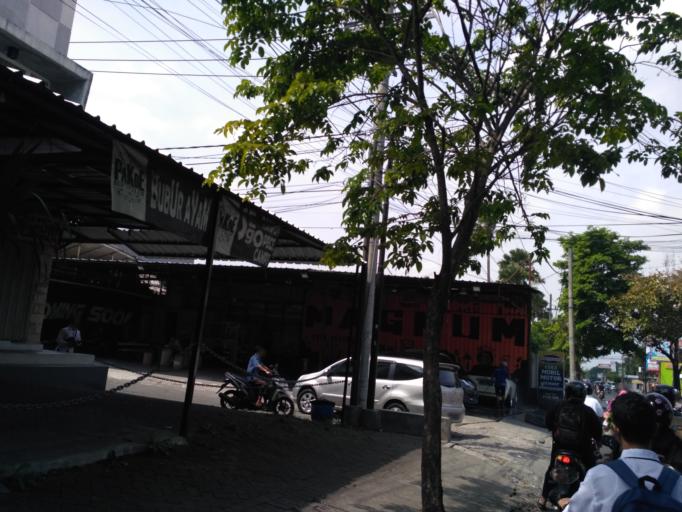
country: ID
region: East Java
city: Malang
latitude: -7.9308
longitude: 112.6103
